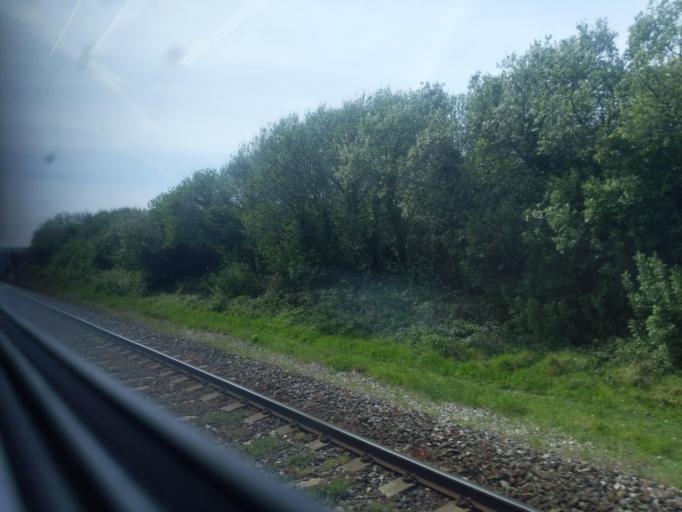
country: GB
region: England
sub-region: Cornwall
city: Marazion
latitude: 50.1309
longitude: -5.4848
